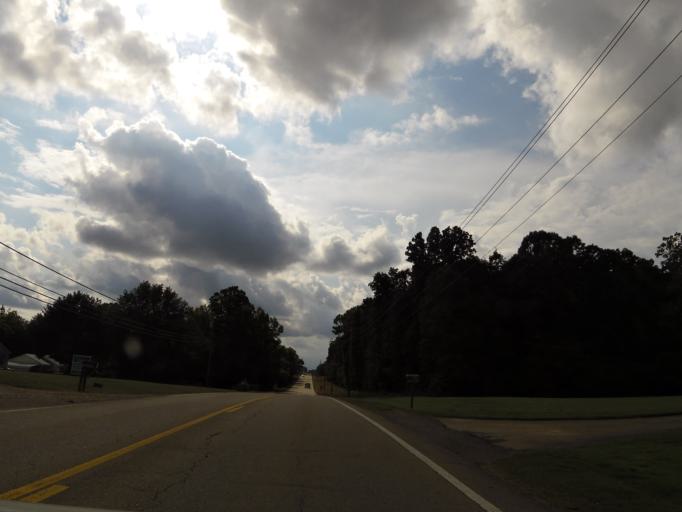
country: US
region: Mississippi
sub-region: Alcorn County
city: Farmington
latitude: 34.9816
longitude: -88.4699
